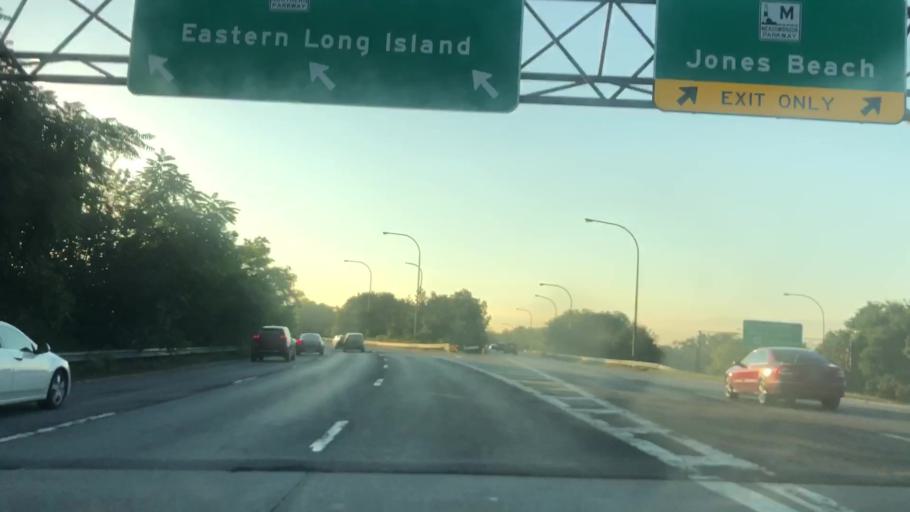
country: US
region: New York
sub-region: Nassau County
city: Carle Place
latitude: 40.7564
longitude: -73.6209
